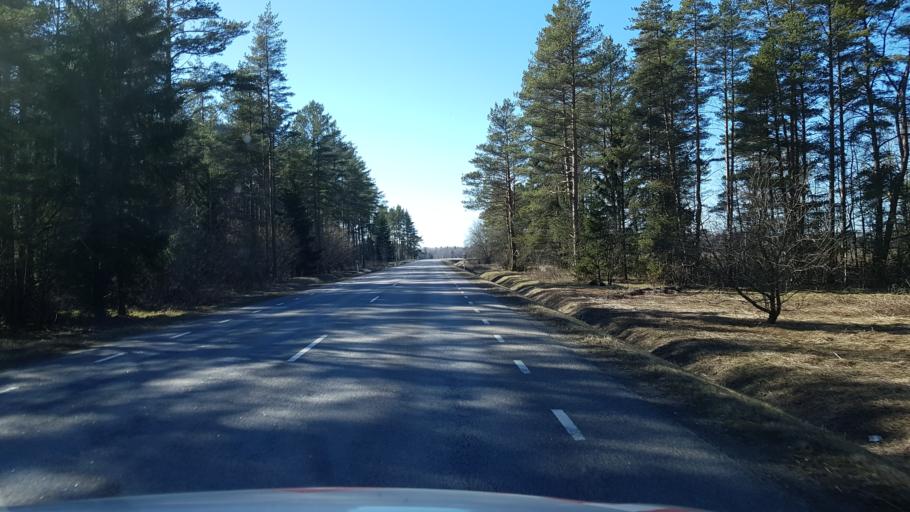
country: EE
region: Laeaene-Virumaa
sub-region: Viru-Nigula vald
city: Kunda
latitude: 59.3600
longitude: 26.6308
